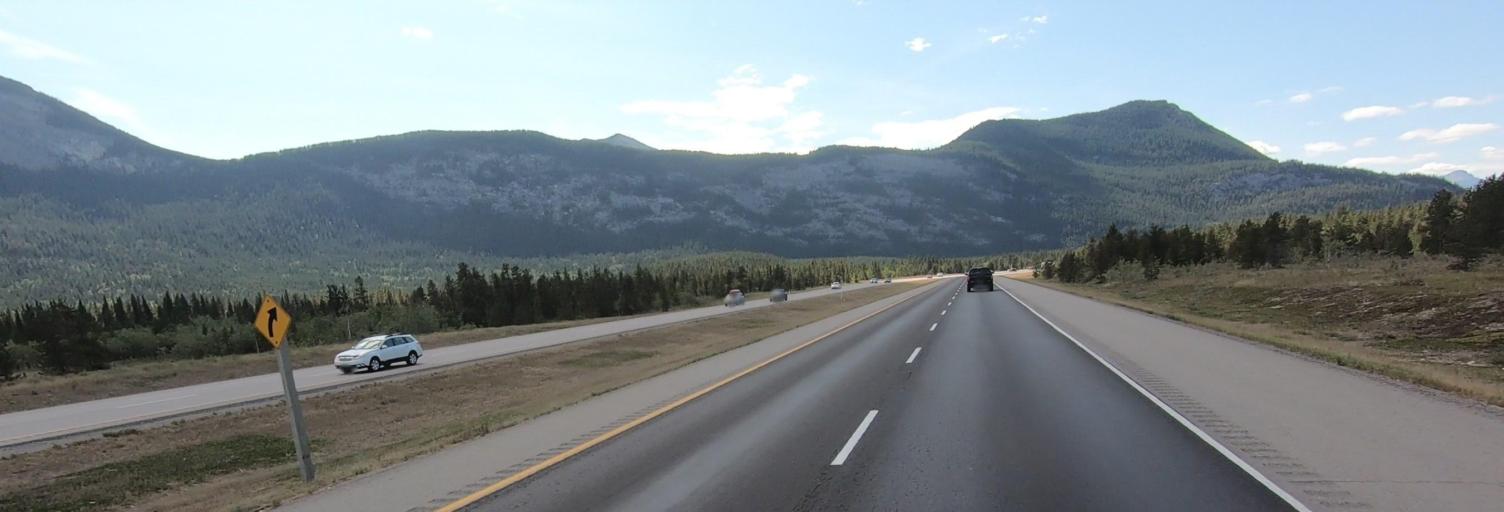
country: CA
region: Alberta
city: Canmore
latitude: 51.0690
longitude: -115.0829
